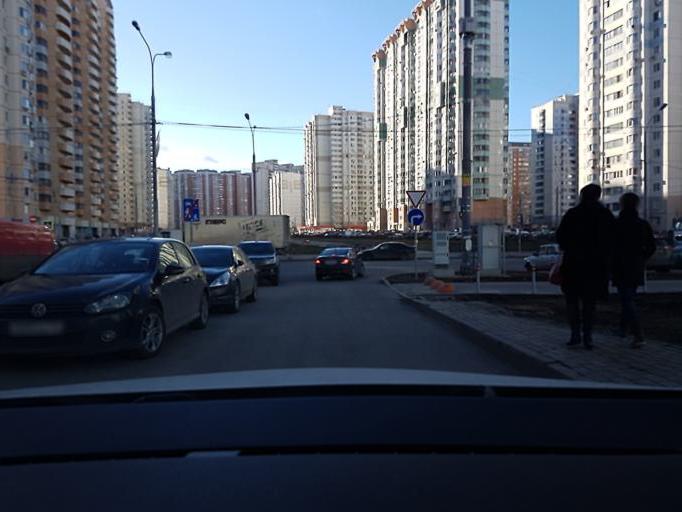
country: RU
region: Moskovskaya
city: Pavshino
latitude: 55.8175
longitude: 37.3738
